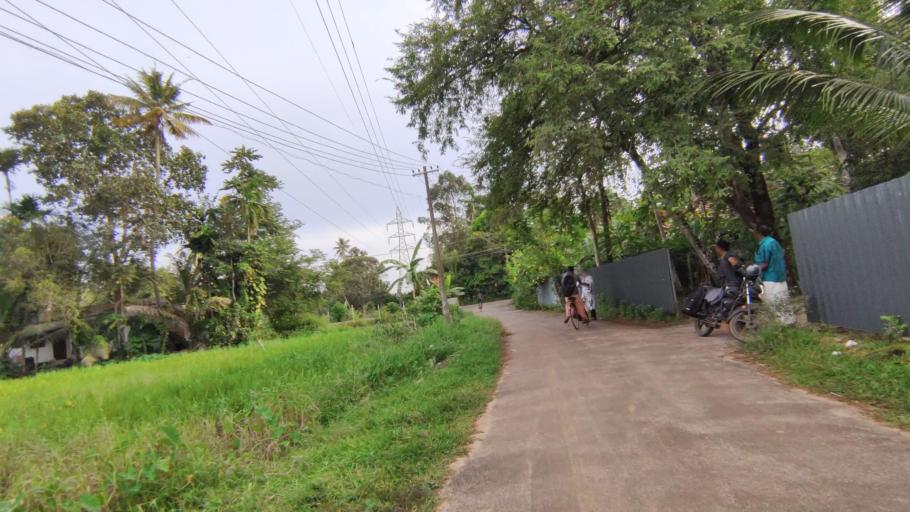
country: IN
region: Kerala
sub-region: Alappuzha
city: Shertallai
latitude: 9.6205
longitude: 76.3349
